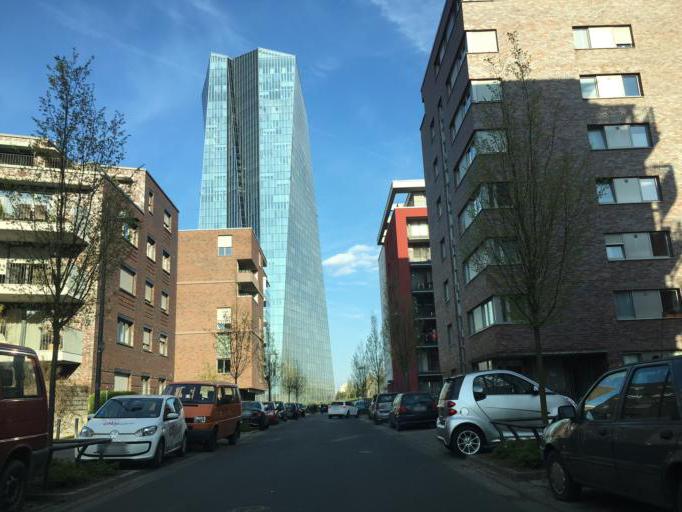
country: DE
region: Hesse
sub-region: Regierungsbezirk Darmstadt
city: Frankfurt am Main
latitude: 50.1089
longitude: 8.6988
